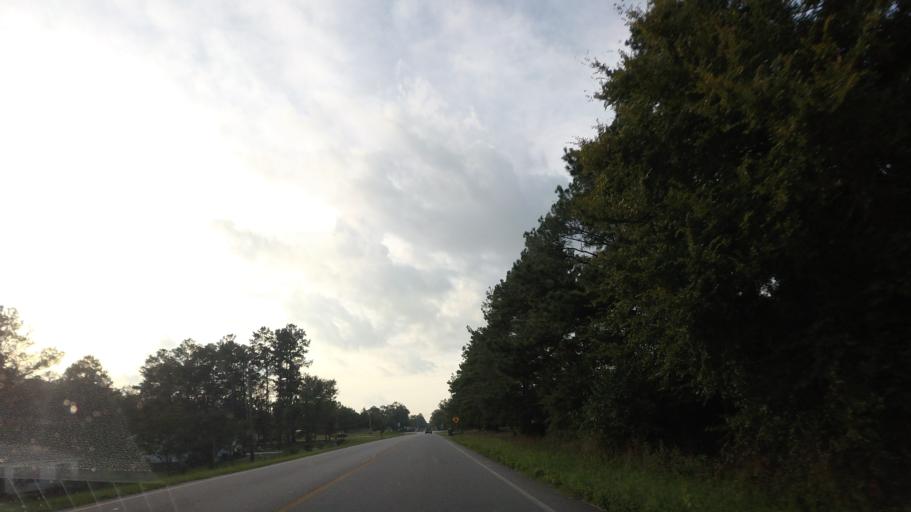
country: US
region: Georgia
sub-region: Wilkinson County
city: Gordon
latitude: 32.8929
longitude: -83.3579
